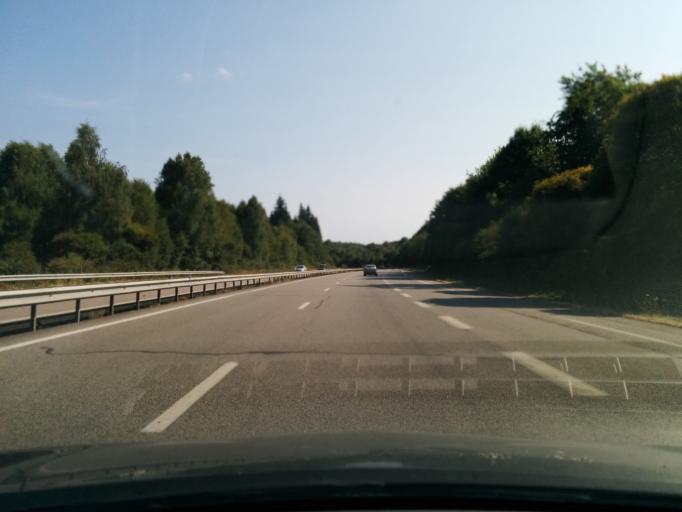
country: FR
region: Limousin
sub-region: Departement de la Haute-Vienne
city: Bonnac-la-Cote
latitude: 45.9357
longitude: 1.3041
